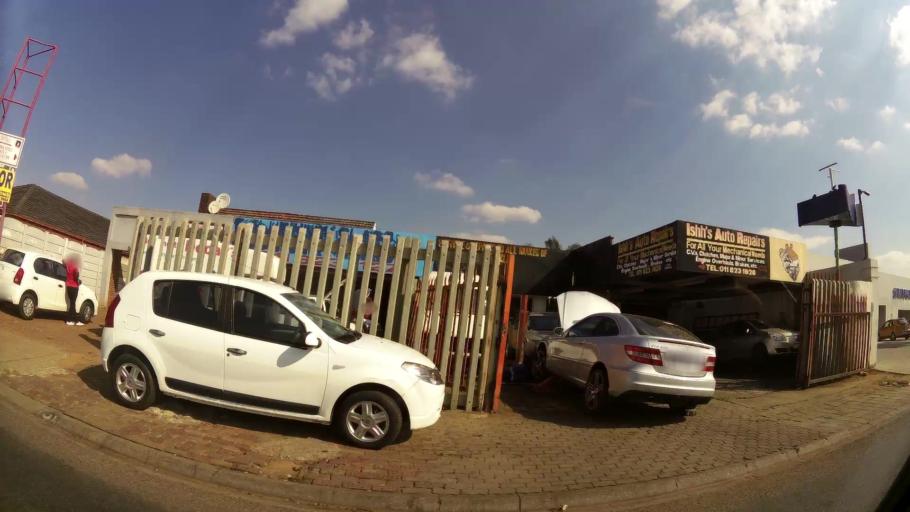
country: ZA
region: Gauteng
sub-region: Ekurhuleni Metropolitan Municipality
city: Boksburg
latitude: -26.1951
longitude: 28.2427
